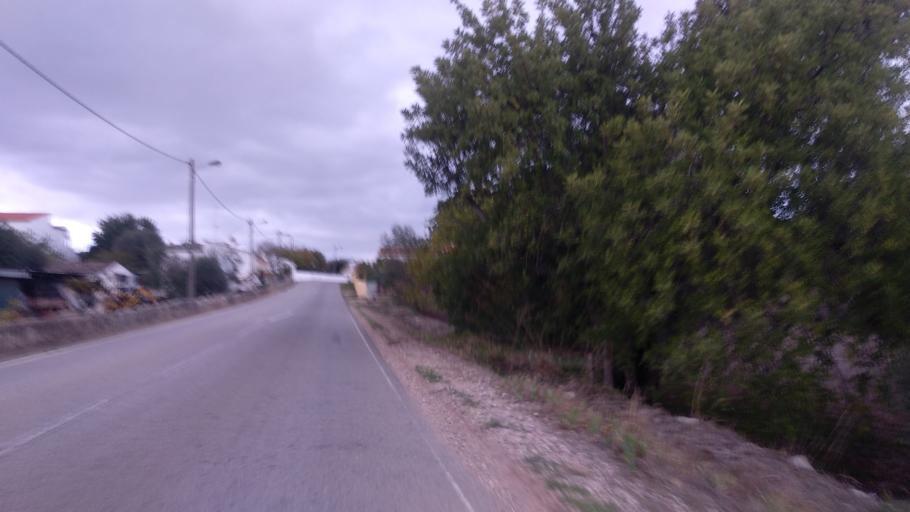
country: PT
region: Faro
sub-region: Sao Bras de Alportel
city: Sao Bras de Alportel
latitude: 37.1693
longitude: -7.9075
